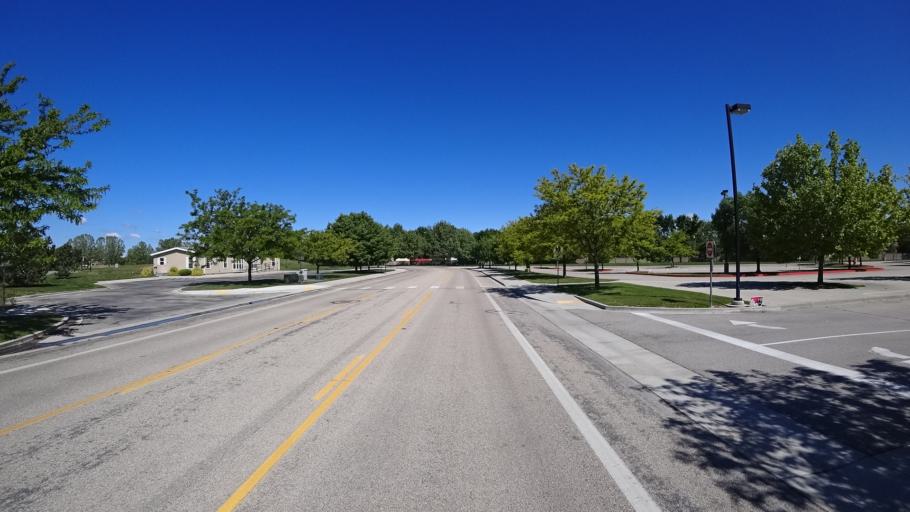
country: US
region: Idaho
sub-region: Ada County
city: Meridian
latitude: 43.6401
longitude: -116.3697
